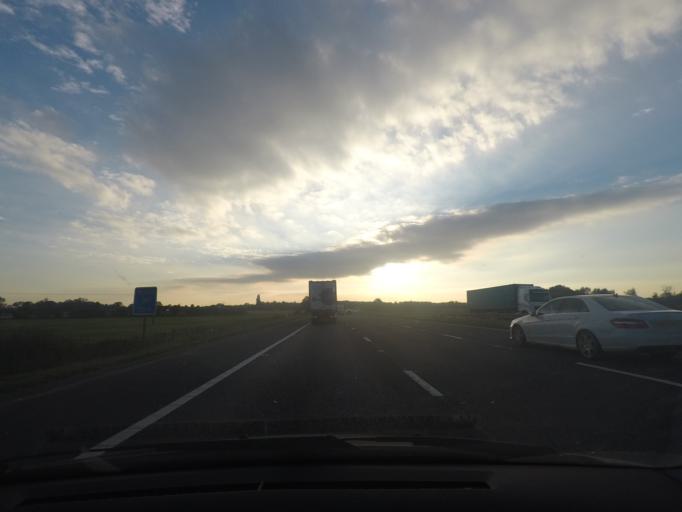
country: GB
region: England
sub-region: North Lincolnshire
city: Brigg
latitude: 53.5558
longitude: -0.5082
